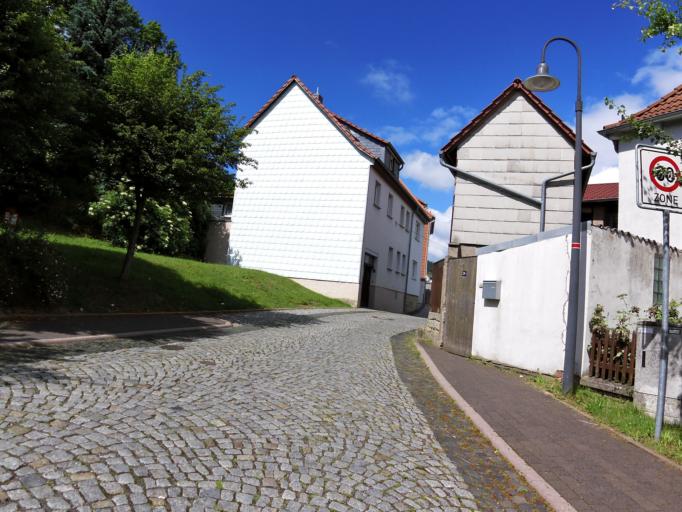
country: DE
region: Thuringia
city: Creuzburg
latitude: 51.0527
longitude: 10.2452
